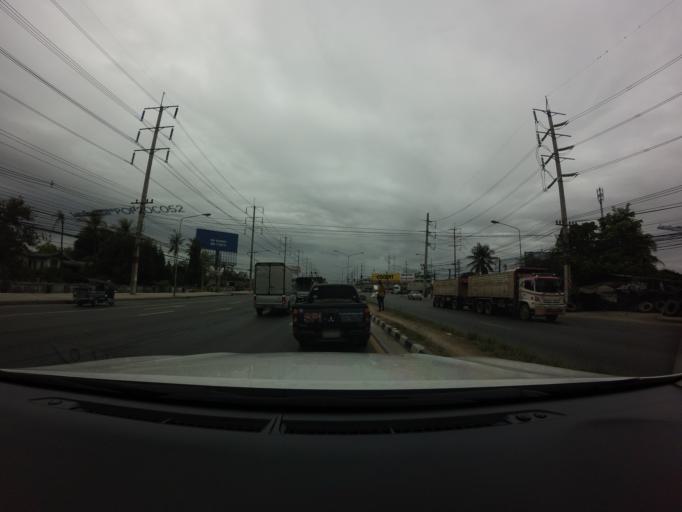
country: TH
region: Chachoengsao
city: Chachoengsao
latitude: 13.6584
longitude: 101.0486
